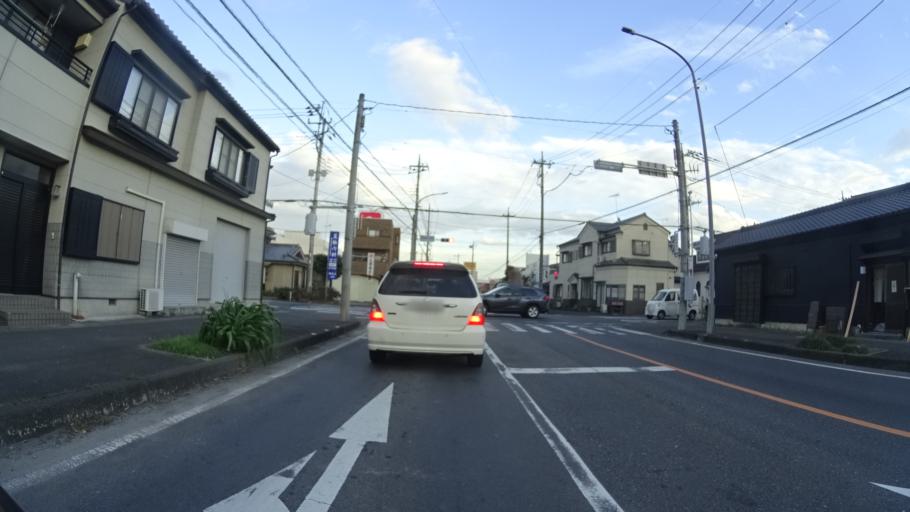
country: JP
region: Tochigi
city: Tochigi
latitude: 36.3905
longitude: 139.7342
